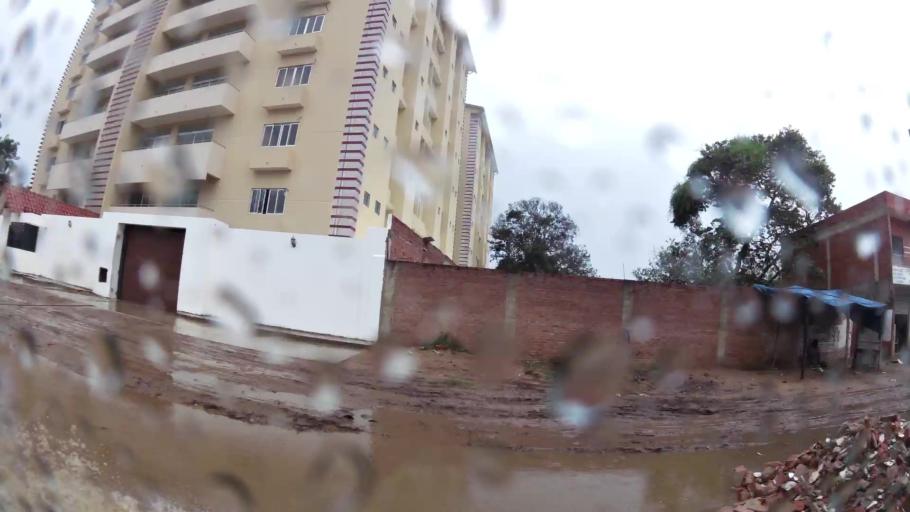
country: BO
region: Santa Cruz
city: Santa Cruz de la Sierra
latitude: -17.8031
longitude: -63.2213
